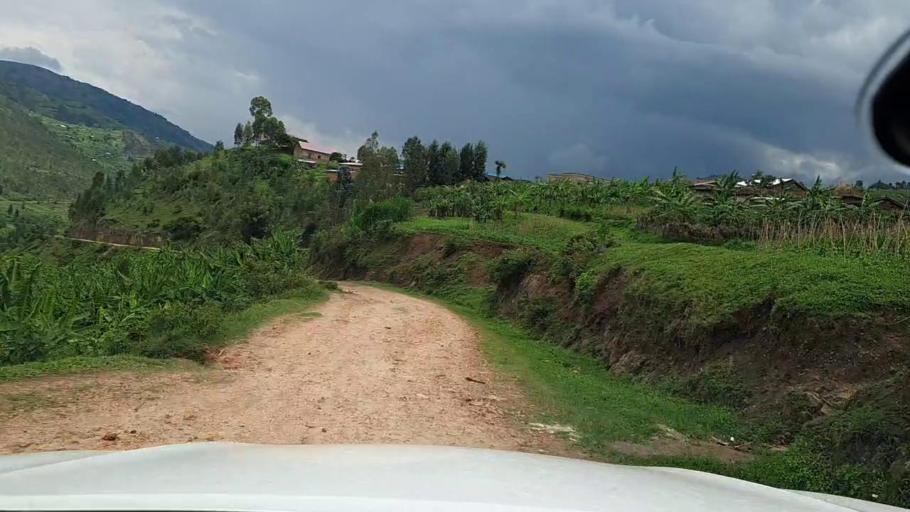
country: RW
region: Western Province
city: Kibuye
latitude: -2.0713
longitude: 29.4297
